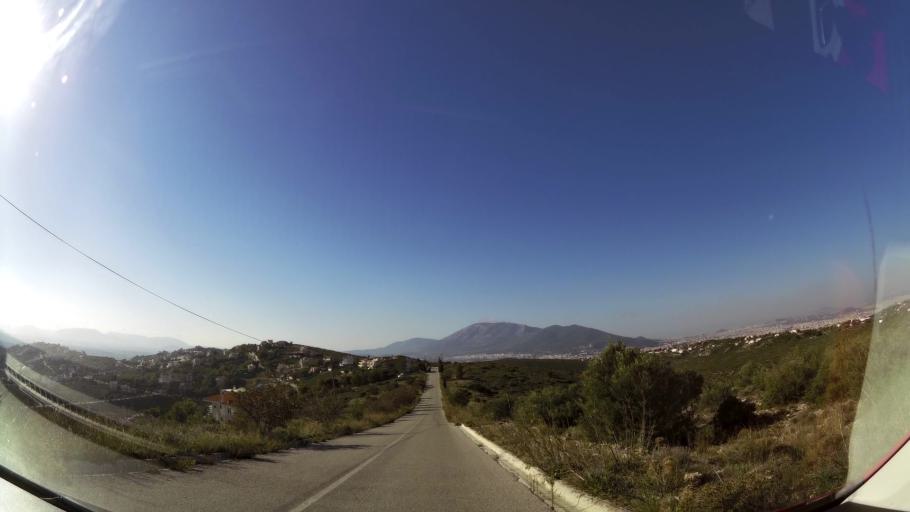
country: GR
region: Attica
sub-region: Nomarchia Anatolikis Attikis
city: Dhrafi
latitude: 38.0380
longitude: 23.8941
